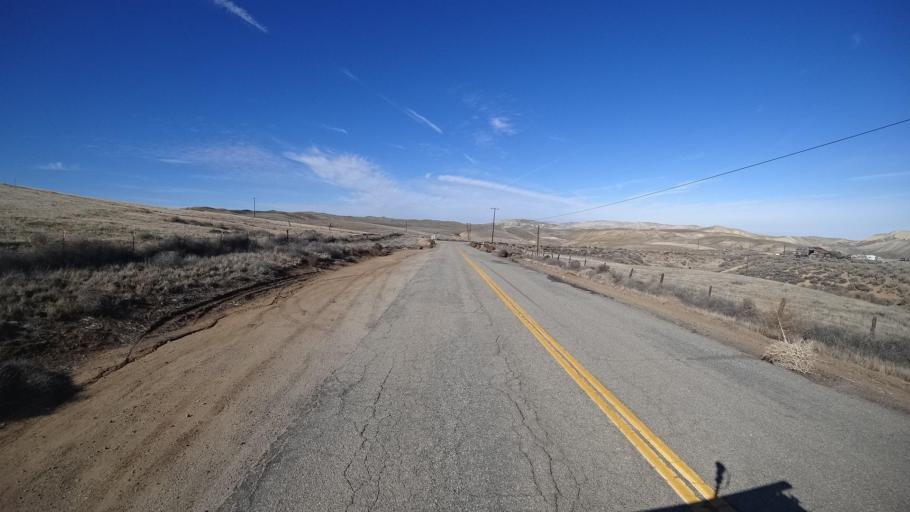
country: US
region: California
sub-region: Kern County
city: Maricopa
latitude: 34.9601
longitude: -119.4461
